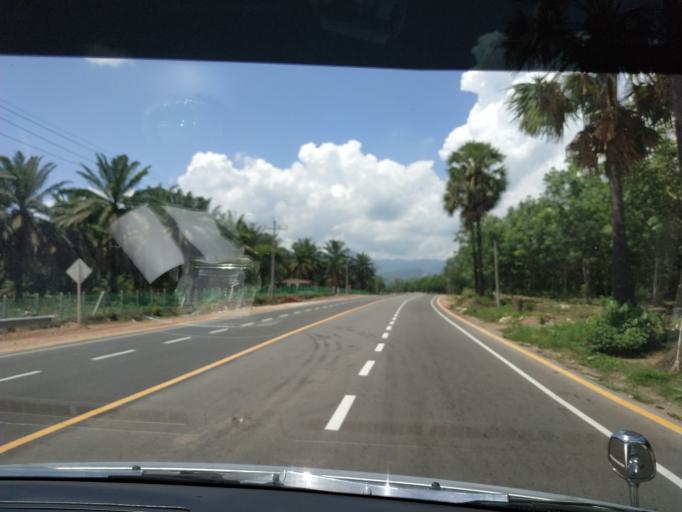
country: MM
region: Mon
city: Kyaikto
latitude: 17.3712
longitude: 97.0499
